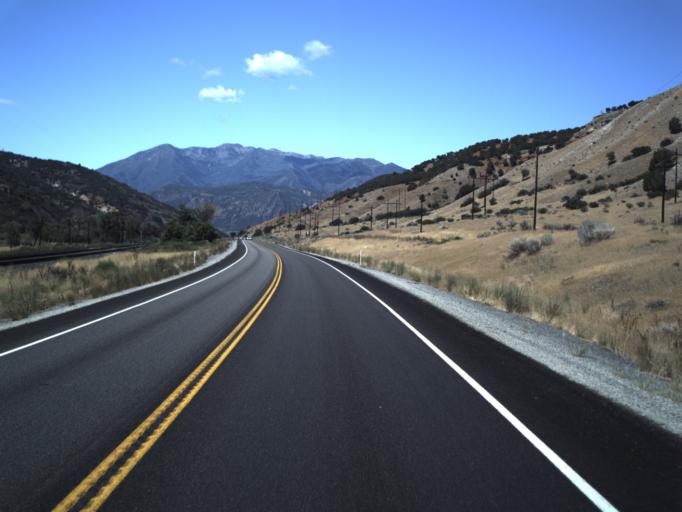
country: US
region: Utah
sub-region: Utah County
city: Mapleton
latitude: 39.9975
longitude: -111.4174
